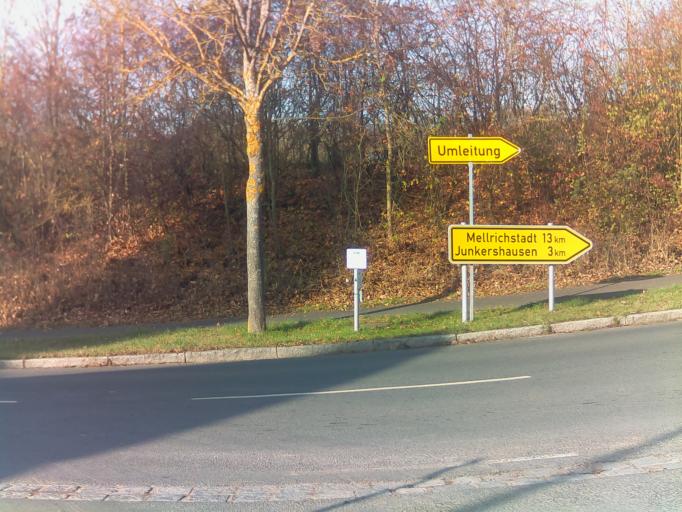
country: DE
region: Bavaria
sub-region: Regierungsbezirk Unterfranken
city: Wuelfershausen
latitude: 50.3335
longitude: 10.3420
